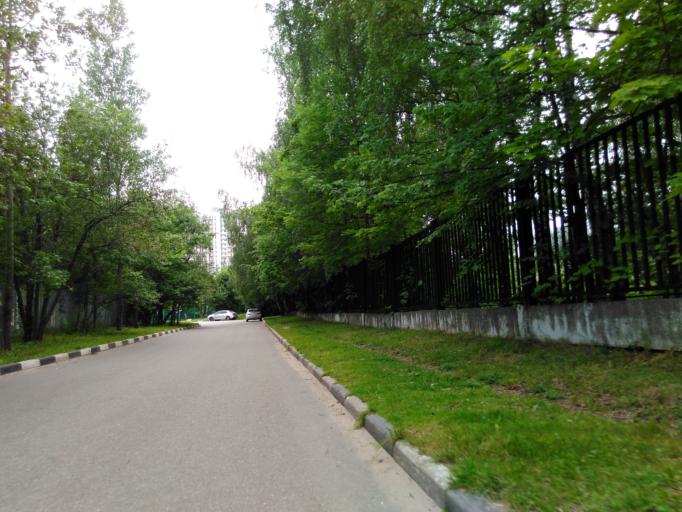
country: RU
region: Moscow
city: Yasenevo
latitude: 55.6165
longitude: 37.5330
